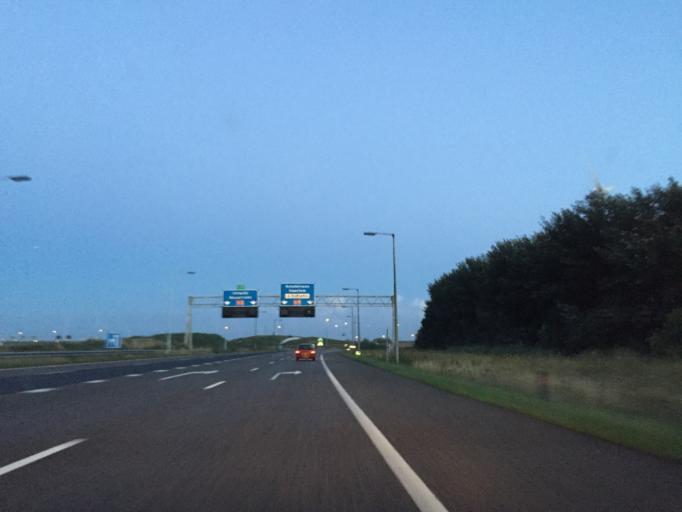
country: NL
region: North Holland
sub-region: Gemeente Amsterdam
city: Amsterdam-Zuidoost
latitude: 52.2915
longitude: 4.9425
